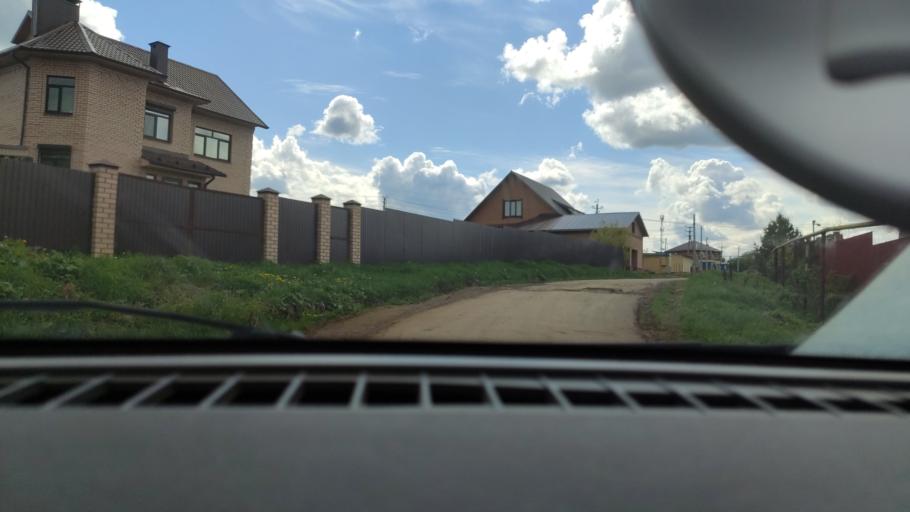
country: RU
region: Perm
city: Ferma
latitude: 57.9441
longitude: 56.3600
